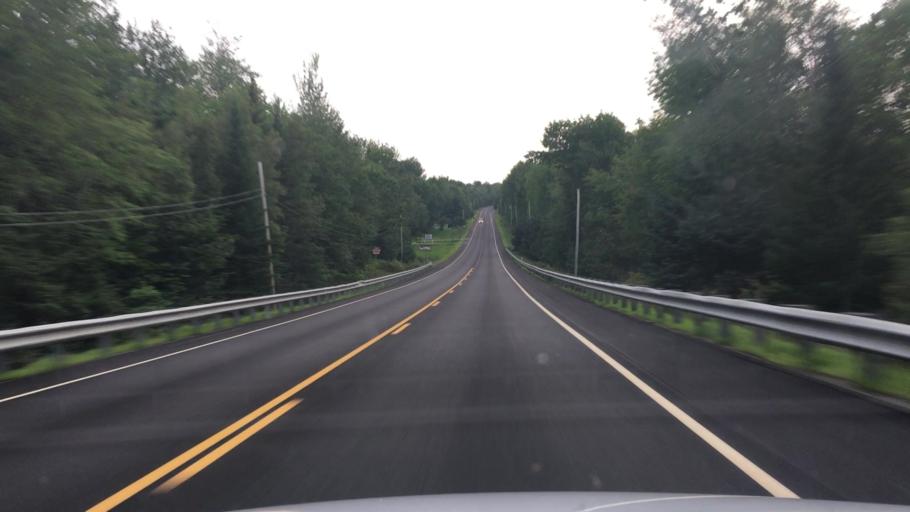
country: US
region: Maine
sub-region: Waldo County
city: Searsmont
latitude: 44.4033
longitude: -69.2339
